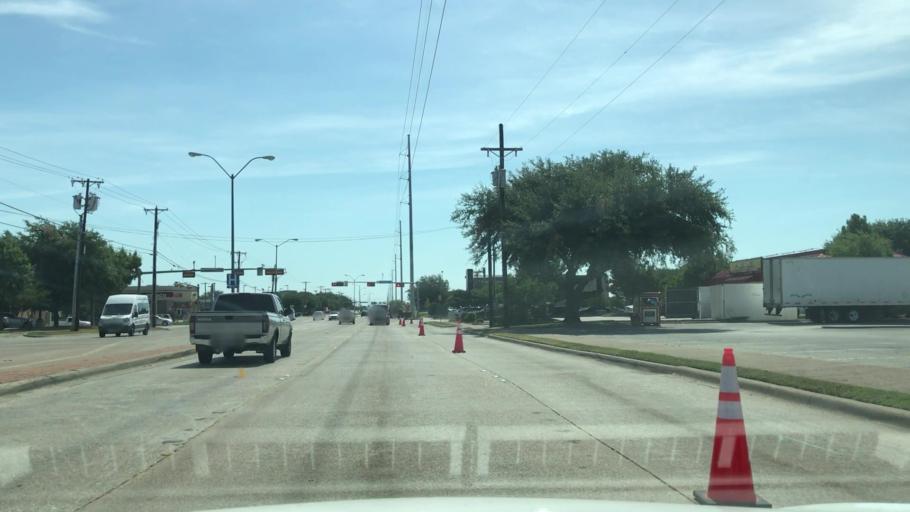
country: US
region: Texas
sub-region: Dallas County
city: Richardson
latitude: 32.9453
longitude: -96.7012
